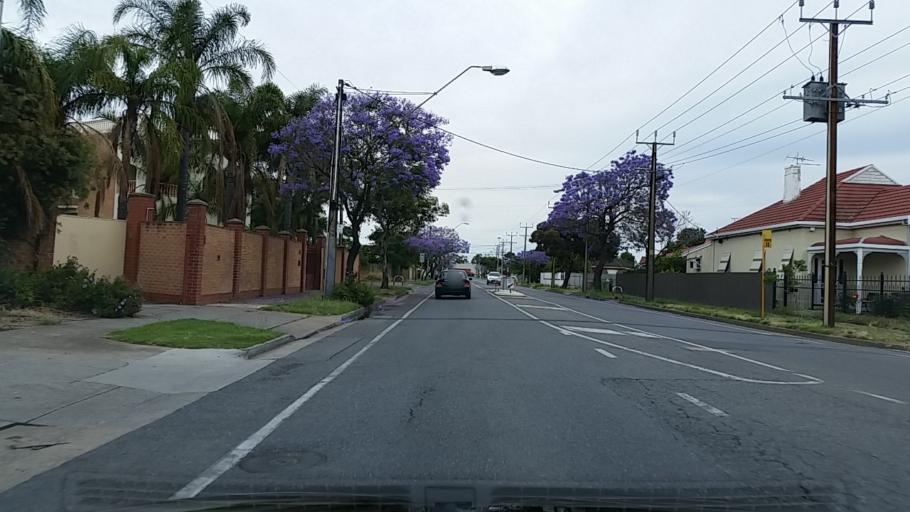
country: AU
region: South Australia
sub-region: Charles Sturt
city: Woodville
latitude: -34.8809
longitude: 138.5499
